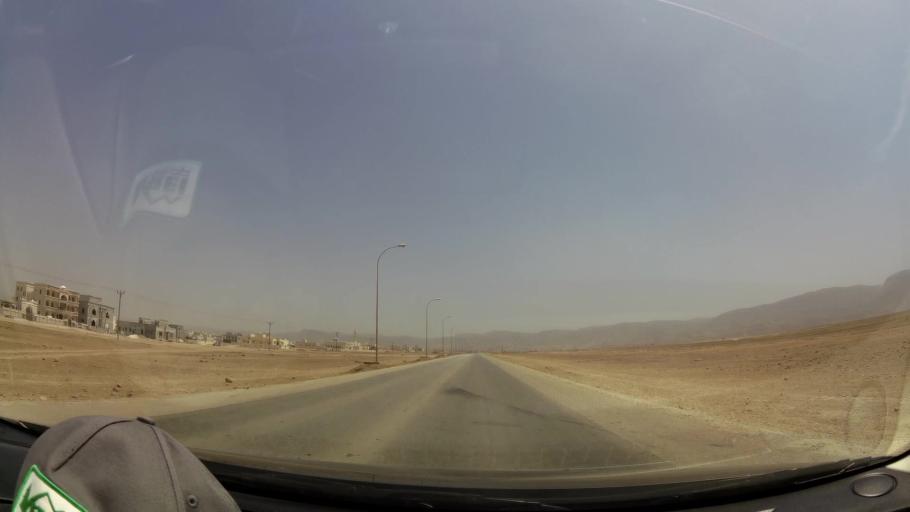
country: OM
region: Zufar
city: Salalah
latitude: 17.0769
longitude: 54.2171
